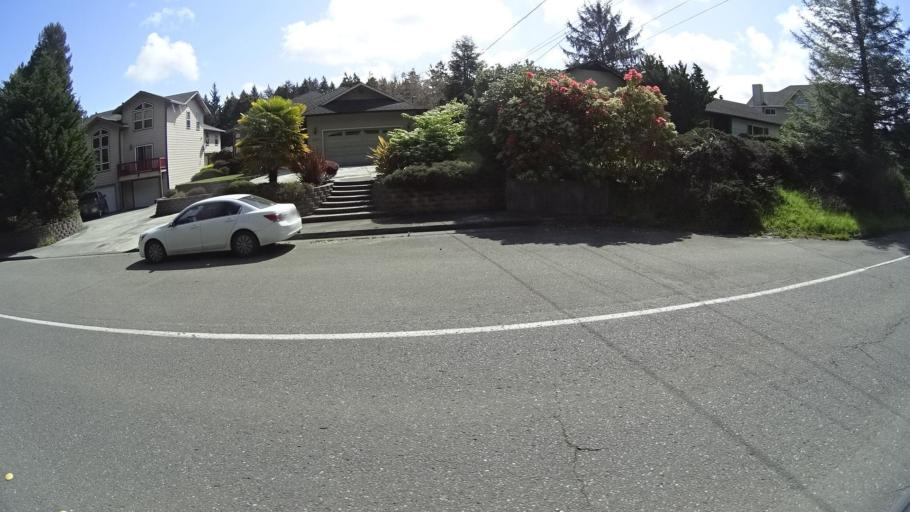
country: US
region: California
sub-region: Humboldt County
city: Pine Hills
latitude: 40.7474
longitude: -124.1477
